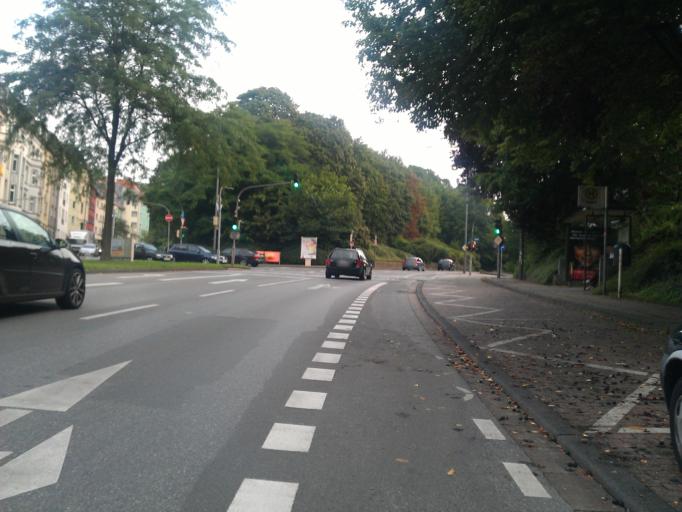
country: DE
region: North Rhine-Westphalia
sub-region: Regierungsbezirk Koln
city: Aachen
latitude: 50.7745
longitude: 6.0723
